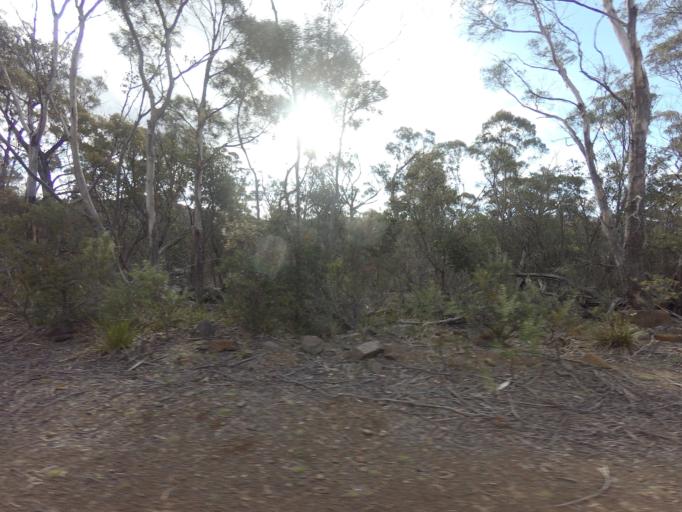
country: AU
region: Tasmania
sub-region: Break O'Day
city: St Helens
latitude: -41.8605
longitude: 148.0237
